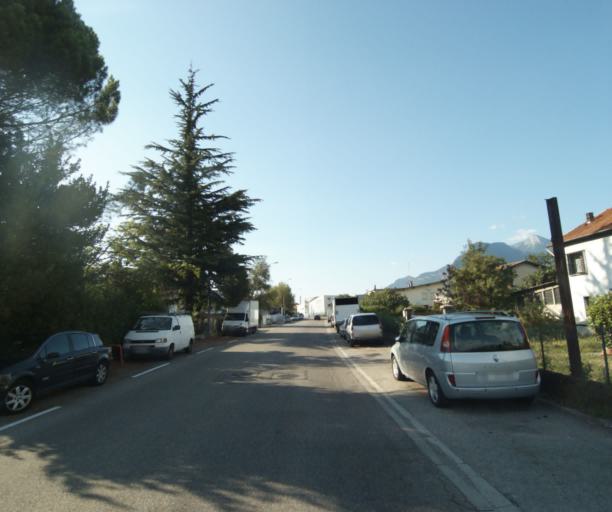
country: FR
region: Rhone-Alpes
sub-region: Departement de l'Isere
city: Fontaine
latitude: 45.2035
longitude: 5.6852
